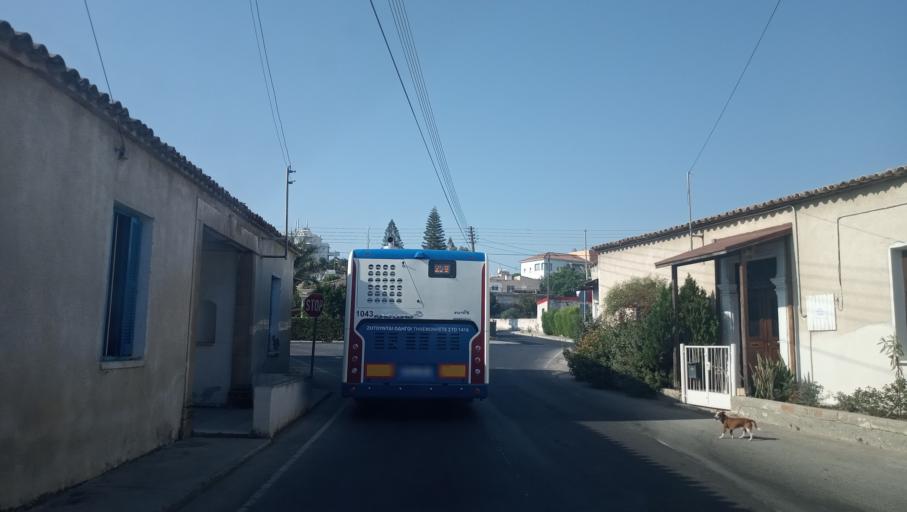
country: CY
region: Lefkosia
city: Geri
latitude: 35.1064
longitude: 33.4234
